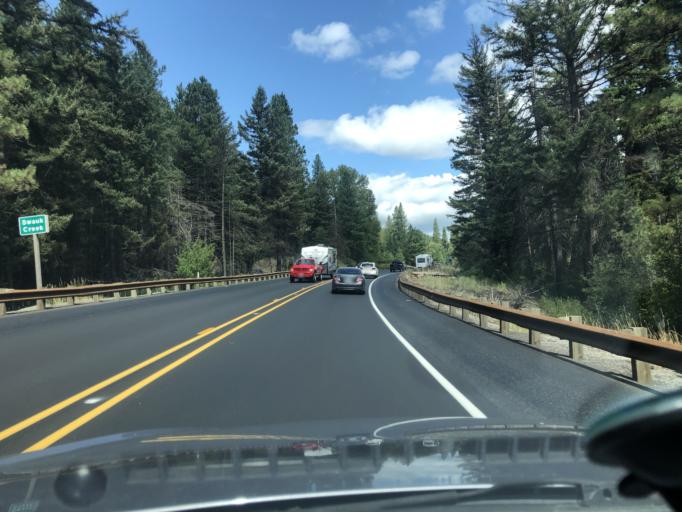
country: US
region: Washington
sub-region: Kittitas County
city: Cle Elum
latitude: 47.2924
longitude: -120.7003
